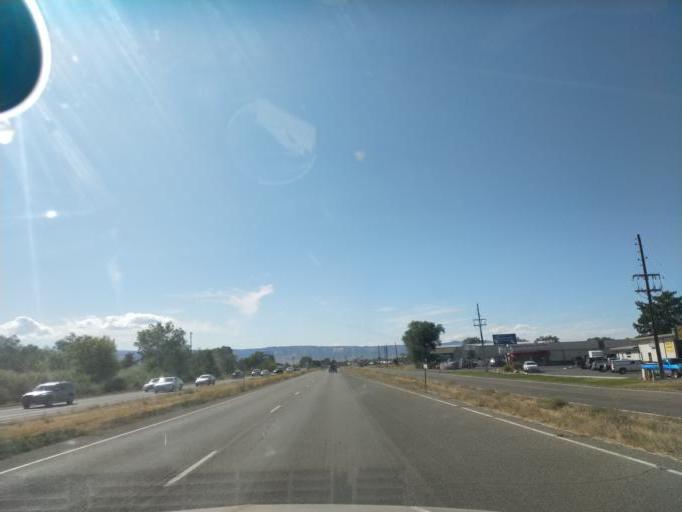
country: US
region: Colorado
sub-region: Mesa County
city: Fruitvale
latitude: 39.0792
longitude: -108.4886
